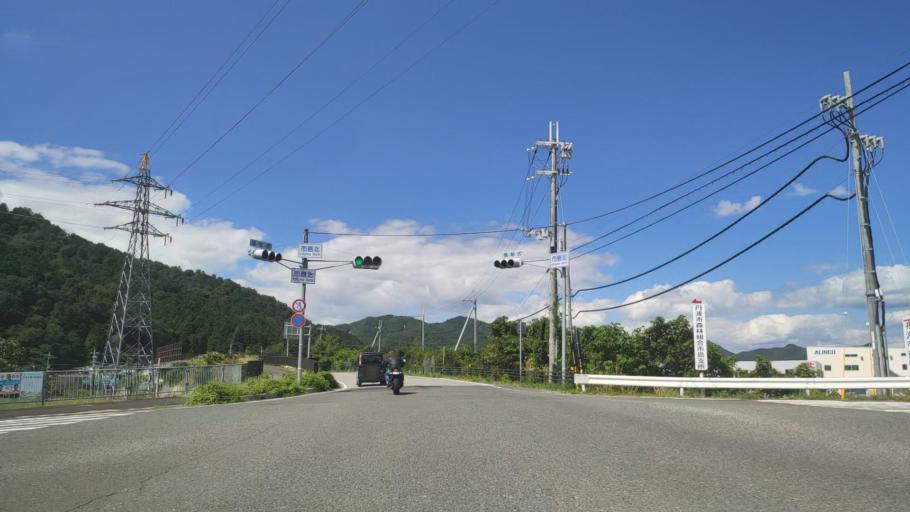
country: JP
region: Kyoto
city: Fukuchiyama
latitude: 35.2160
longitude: 135.1347
